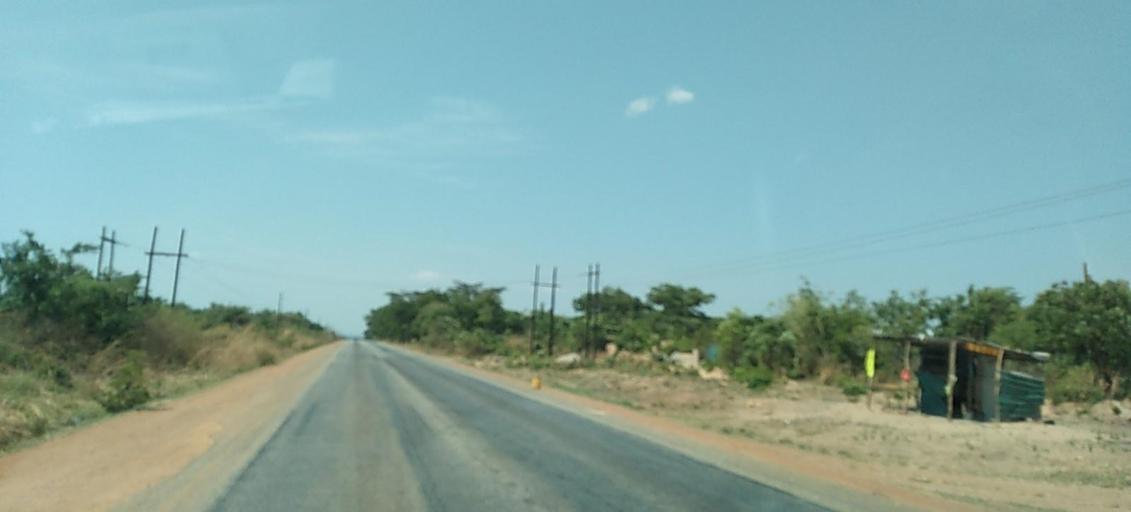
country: ZM
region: Copperbelt
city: Luanshya
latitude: -13.4719
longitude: 28.6725
